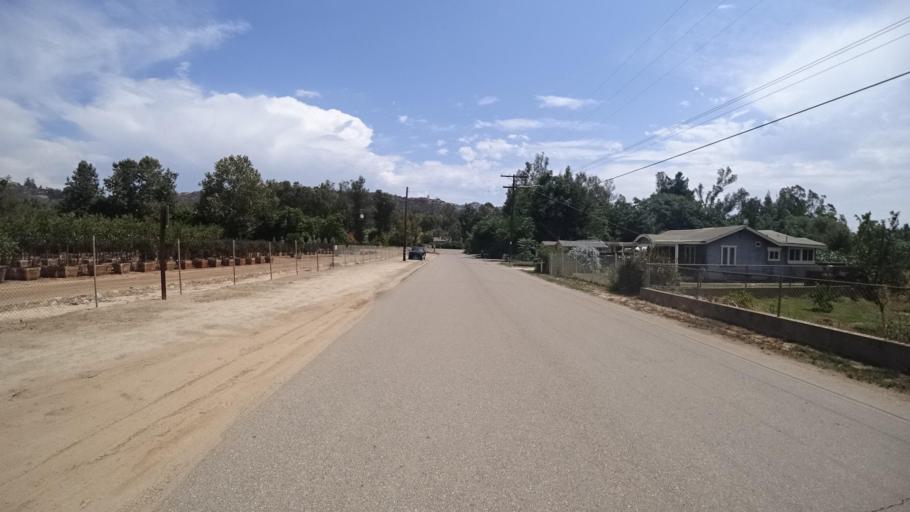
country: US
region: California
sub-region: San Diego County
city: Hidden Meadows
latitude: 33.1818
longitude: -117.0941
